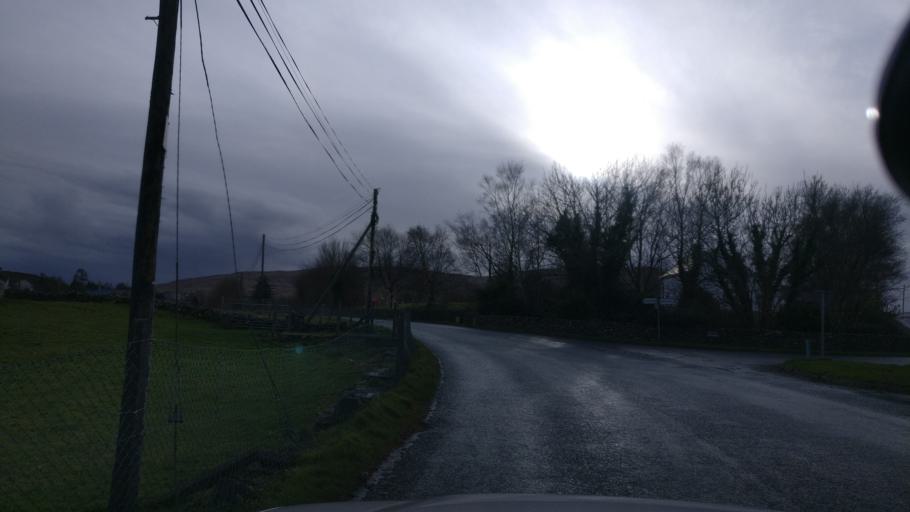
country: IE
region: Connaught
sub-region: County Galway
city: Oughterard
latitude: 53.5579
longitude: -9.4532
